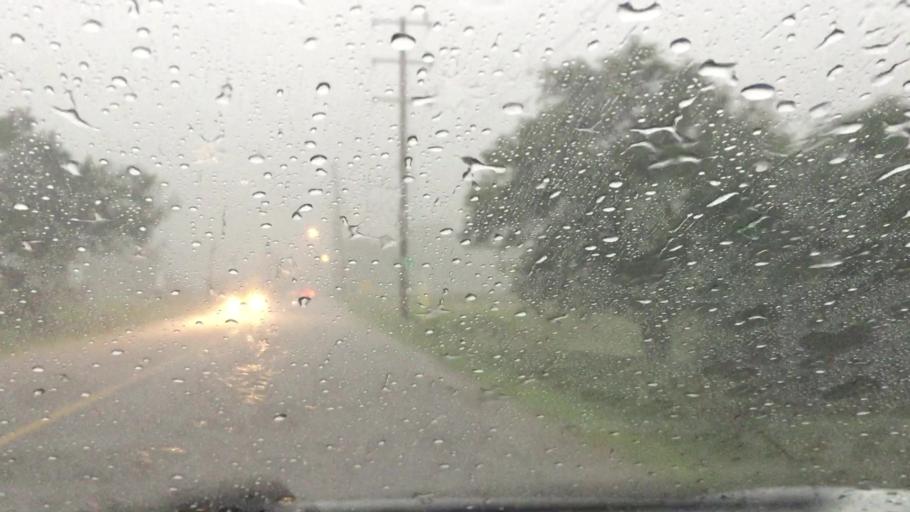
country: CA
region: Ontario
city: Markham
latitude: 43.8641
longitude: -79.2056
